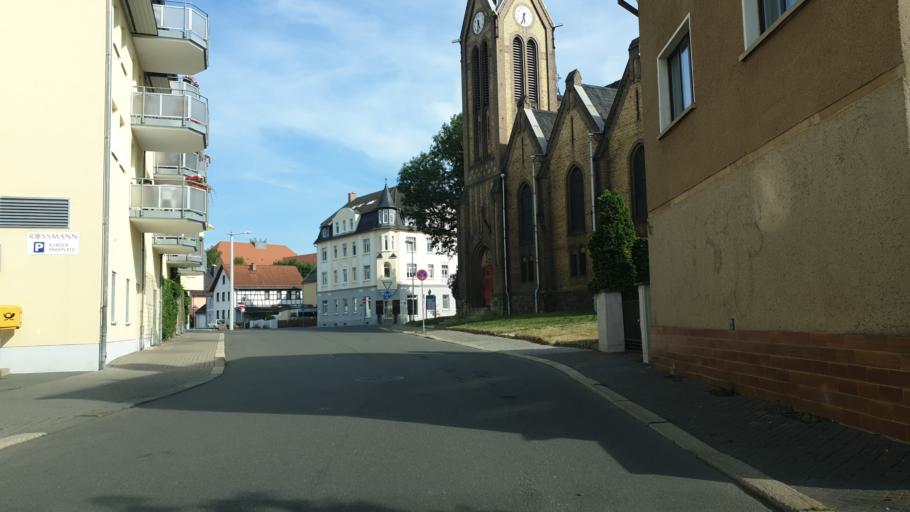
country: DE
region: Thuringia
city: Gera
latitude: 50.8483
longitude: 12.0860
